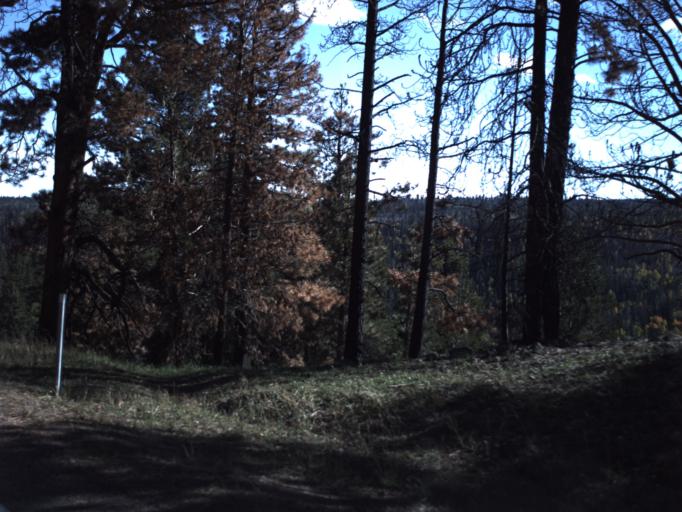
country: US
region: Utah
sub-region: Iron County
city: Parowan
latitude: 37.6530
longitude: -112.7002
